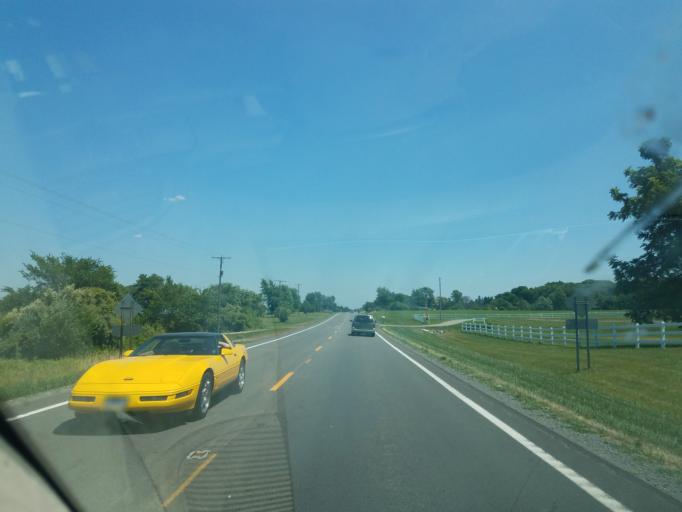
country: US
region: Ohio
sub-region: Hardin County
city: Ada
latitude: 40.7327
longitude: -83.8378
